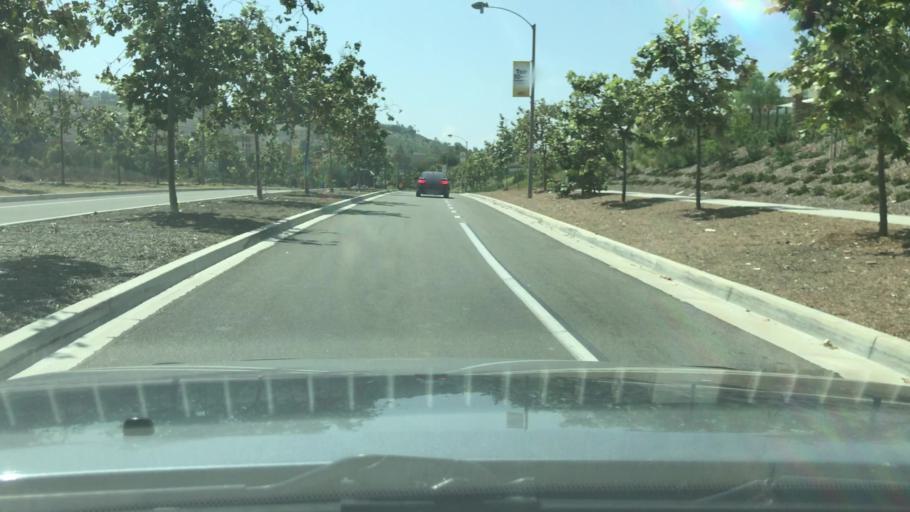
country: US
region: California
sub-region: Orange County
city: San Joaquin Hills
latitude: 33.6369
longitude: -117.8280
